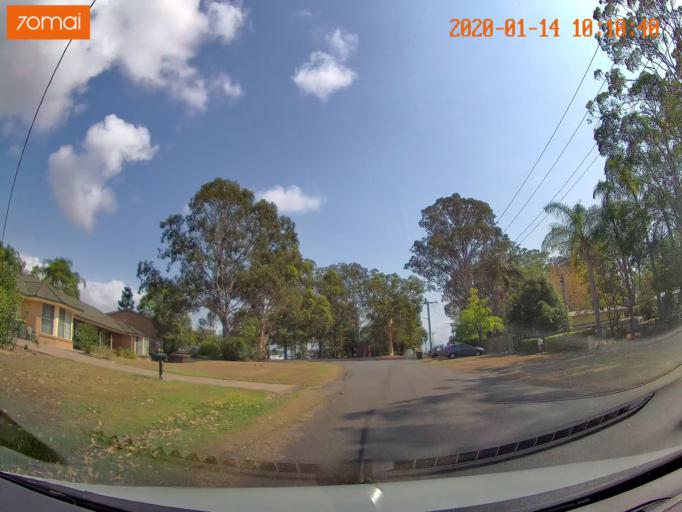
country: AU
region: New South Wales
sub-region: Wyong Shire
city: Kingfisher Shores
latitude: -33.1213
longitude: 151.5360
